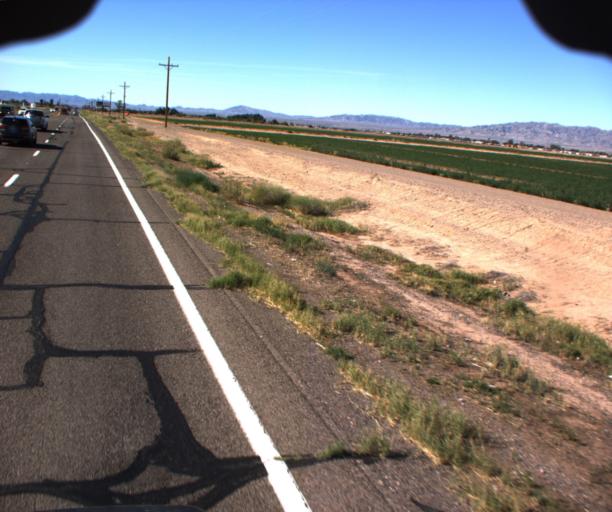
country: US
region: Arizona
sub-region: Mohave County
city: Mohave Valley
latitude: 34.9328
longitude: -114.5980
